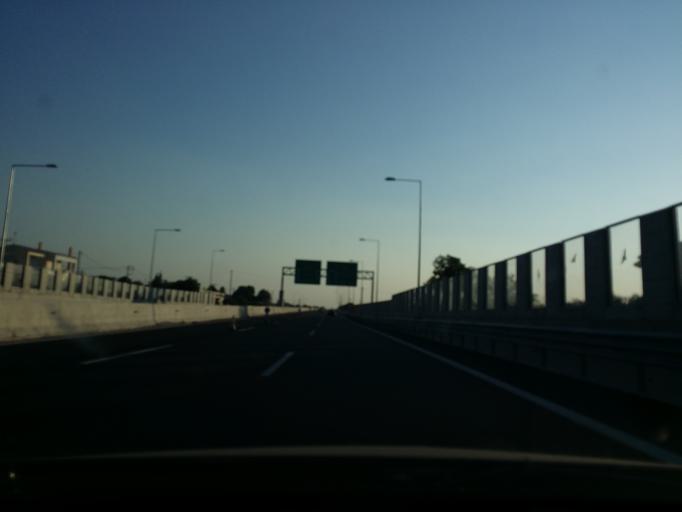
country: GR
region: West Greece
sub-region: Nomos Achaias
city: Rio
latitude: 38.3094
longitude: 21.8127
